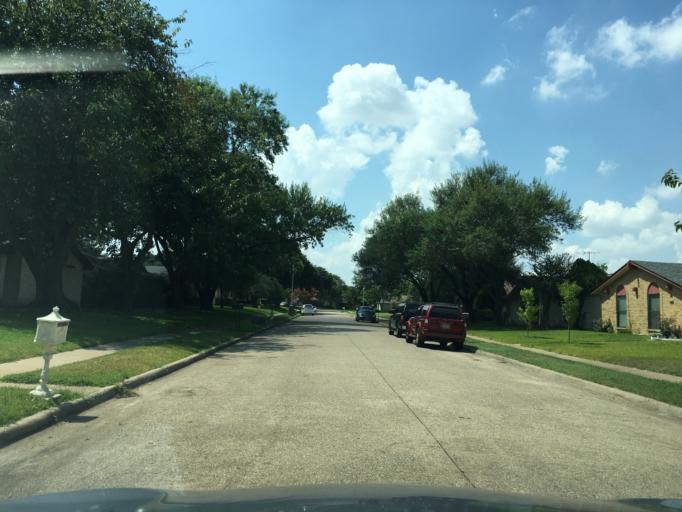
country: US
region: Texas
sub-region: Dallas County
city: Garland
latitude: 32.9428
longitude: -96.6598
